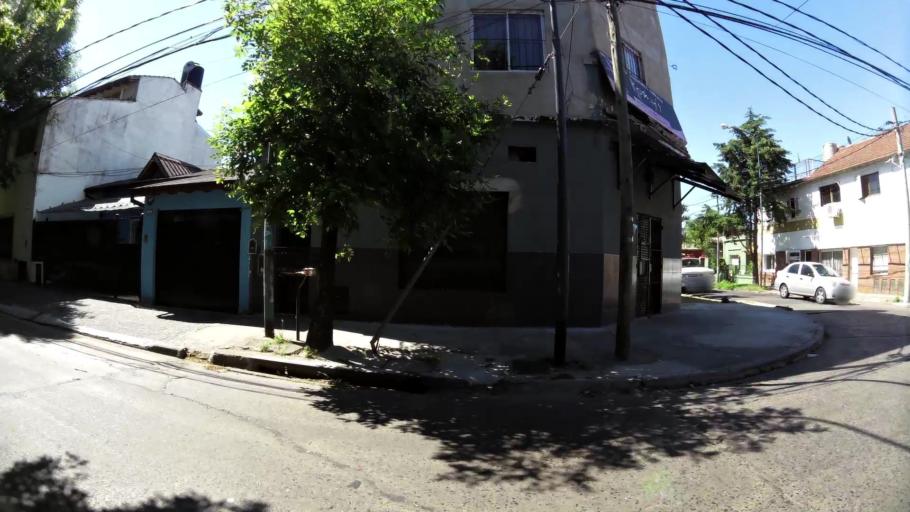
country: AR
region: Buenos Aires
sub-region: Partido de Vicente Lopez
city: Olivos
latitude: -34.5251
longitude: -58.5285
